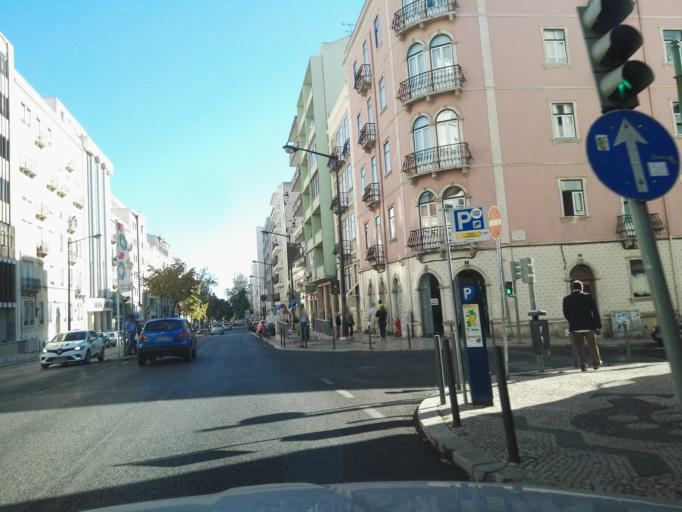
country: PT
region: Lisbon
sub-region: Lisbon
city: Lisbon
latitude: 38.7281
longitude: -9.1348
